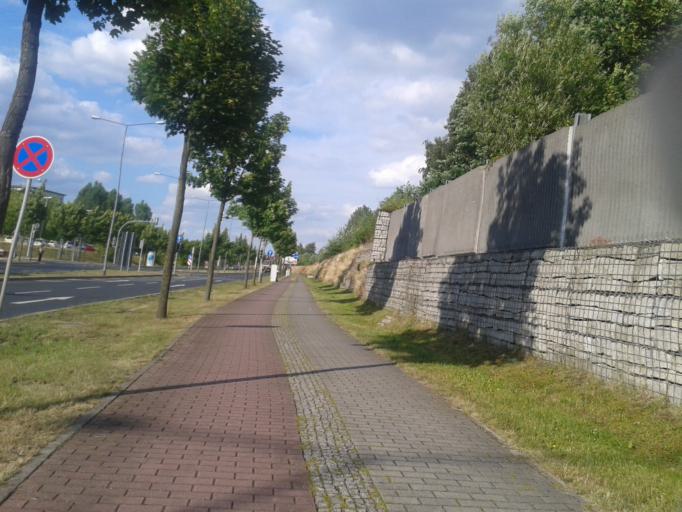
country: DE
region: Saxony
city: Albertstadt
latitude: 51.1209
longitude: 13.7644
